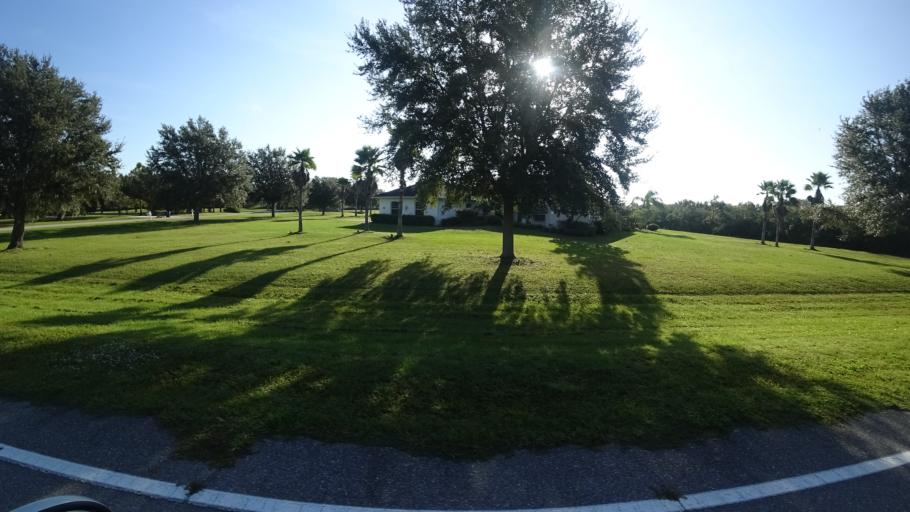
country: US
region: Florida
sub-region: Hillsborough County
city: Sun City Center
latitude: 27.5548
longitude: -82.3537
